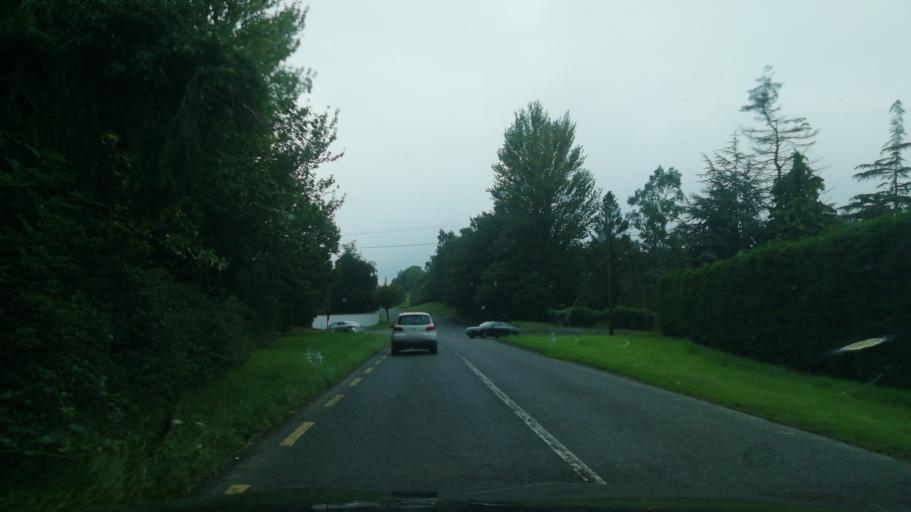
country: IE
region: Munster
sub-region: South Tipperary
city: Cluain Meala
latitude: 52.3836
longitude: -7.6970
